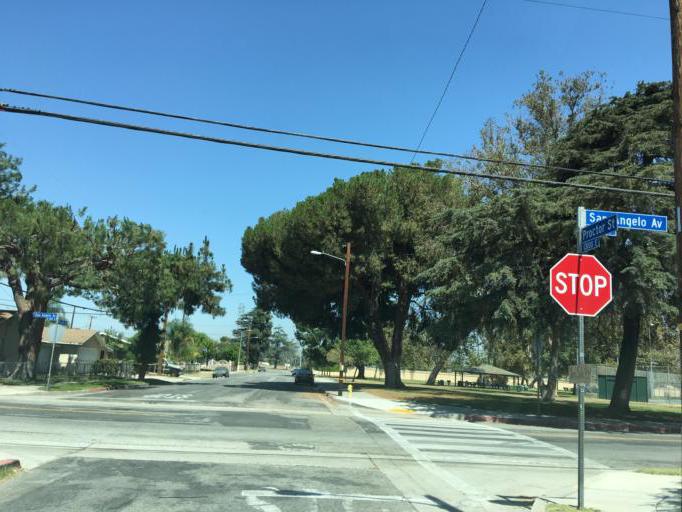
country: US
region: California
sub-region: Los Angeles County
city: Avocado Heights
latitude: 34.0487
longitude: -118.0026
